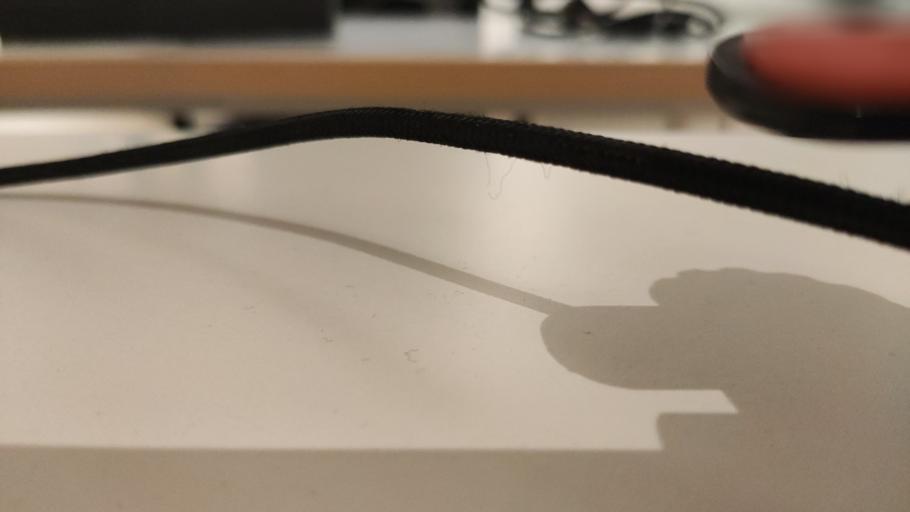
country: RU
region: Moskovskaya
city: Dorokhovo
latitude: 55.4181
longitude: 36.3644
